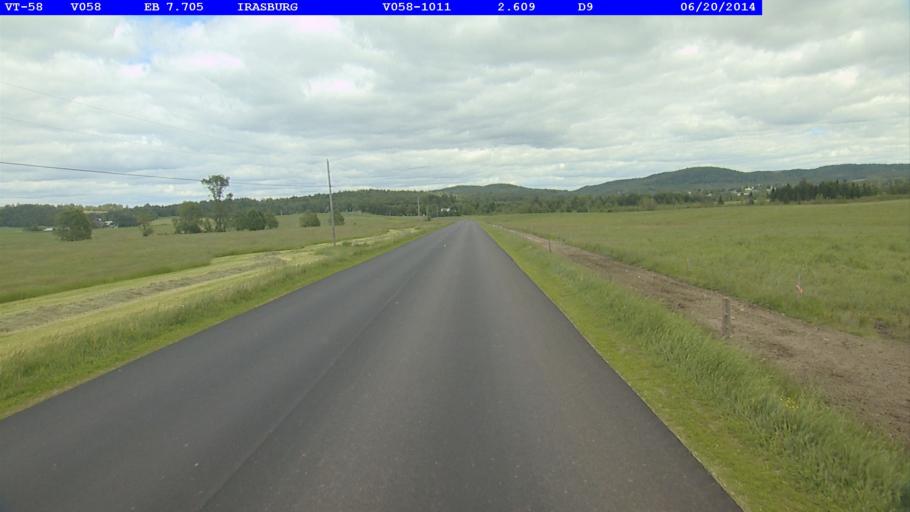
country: US
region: Vermont
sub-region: Orleans County
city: Newport
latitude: 44.8146
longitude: -72.3076
